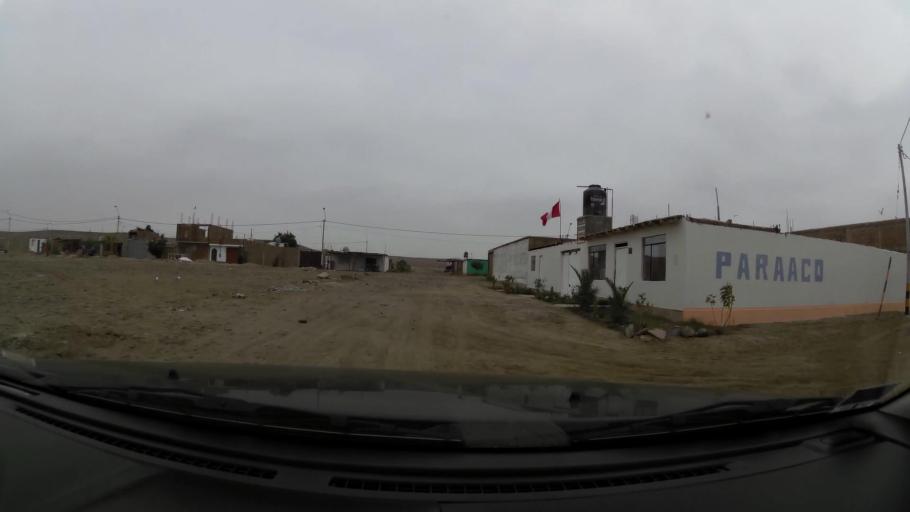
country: PE
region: Ica
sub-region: Provincia de Pisco
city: Paracas
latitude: -13.8346
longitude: -76.2472
